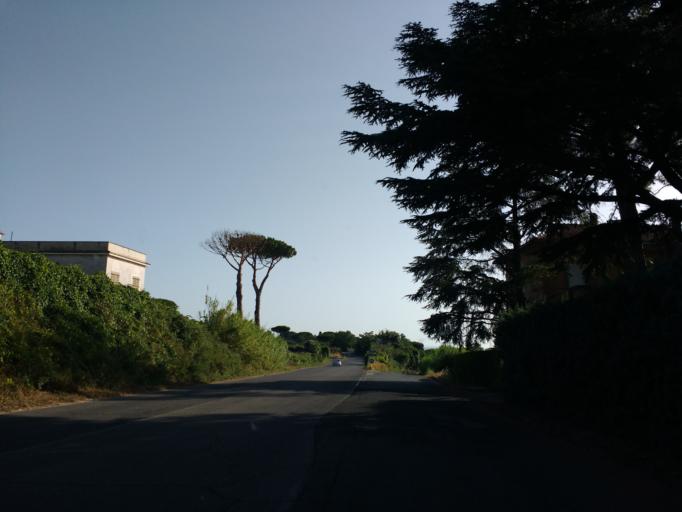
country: IT
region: Latium
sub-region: Citta metropolitana di Roma Capitale
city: Marino
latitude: 41.7555
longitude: 12.6384
